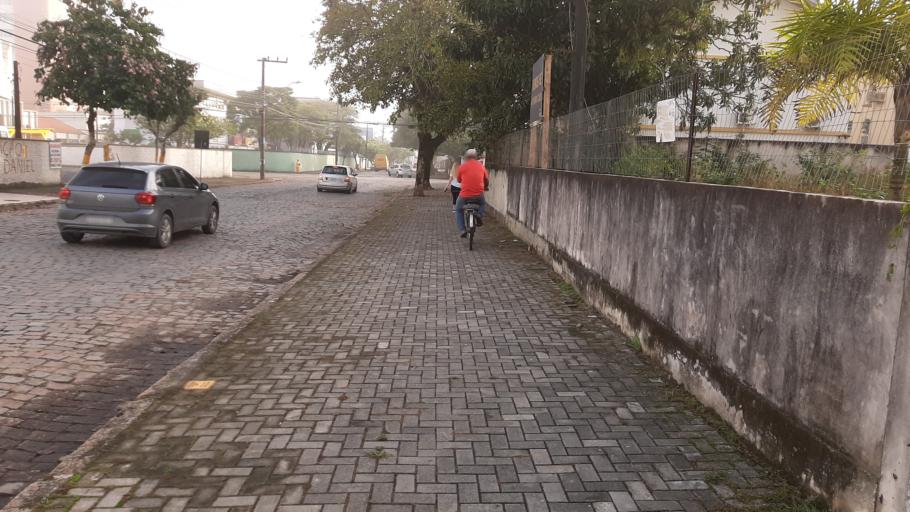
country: BR
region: Santa Catarina
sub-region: Joinville
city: Joinville
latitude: -26.3135
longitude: -48.8394
